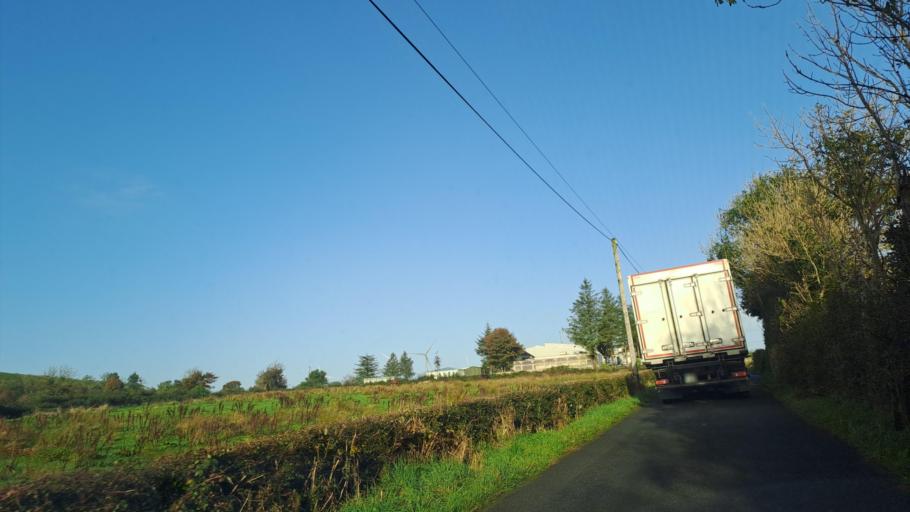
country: IE
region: Ulster
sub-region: County Monaghan
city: Castleblayney
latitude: 54.0776
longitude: -6.8434
